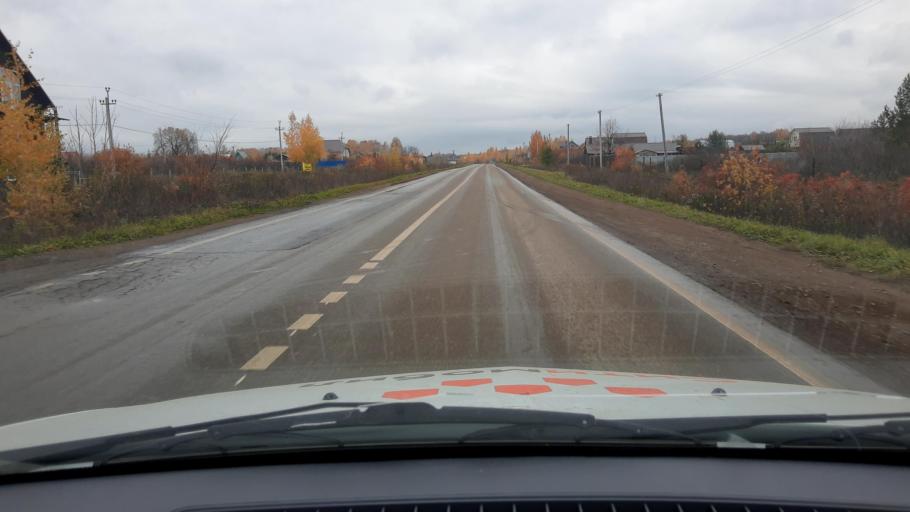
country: RU
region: Bashkortostan
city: Kabakovo
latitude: 54.7143
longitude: 56.1708
